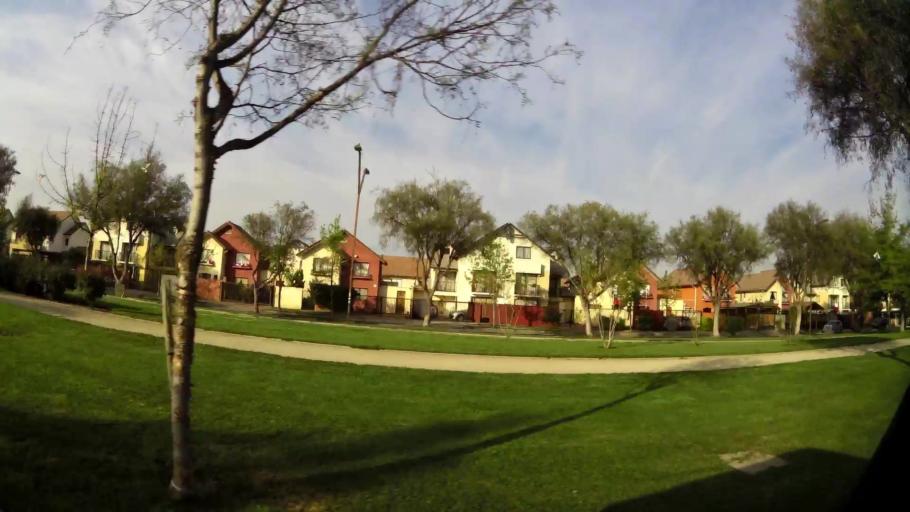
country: CL
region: Santiago Metropolitan
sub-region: Provincia de Maipo
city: San Bernardo
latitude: -33.5616
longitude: -70.7775
